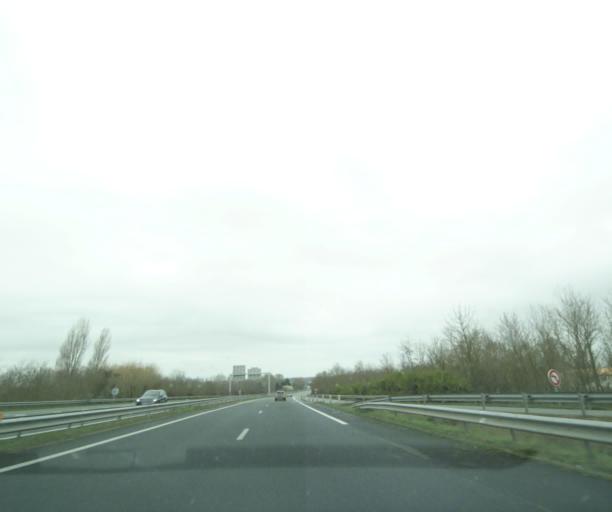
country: FR
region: Poitou-Charentes
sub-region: Departement de la Charente-Maritime
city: Breuil-Magne
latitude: 45.9692
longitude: -0.9829
